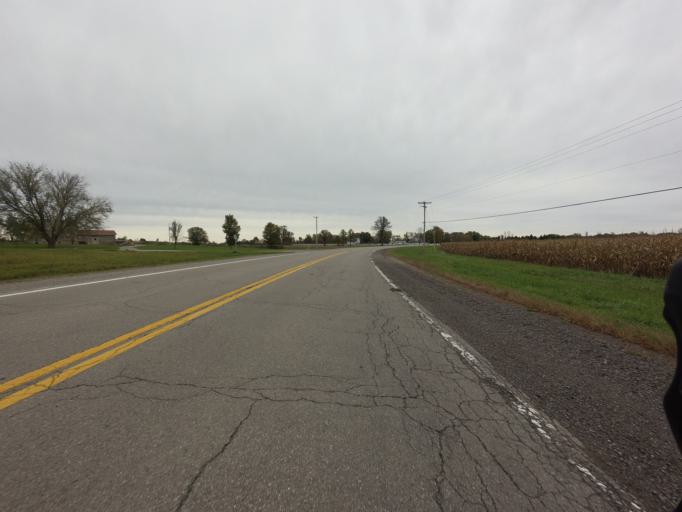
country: CA
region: Ontario
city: Brockville
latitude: 44.6467
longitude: -75.9080
